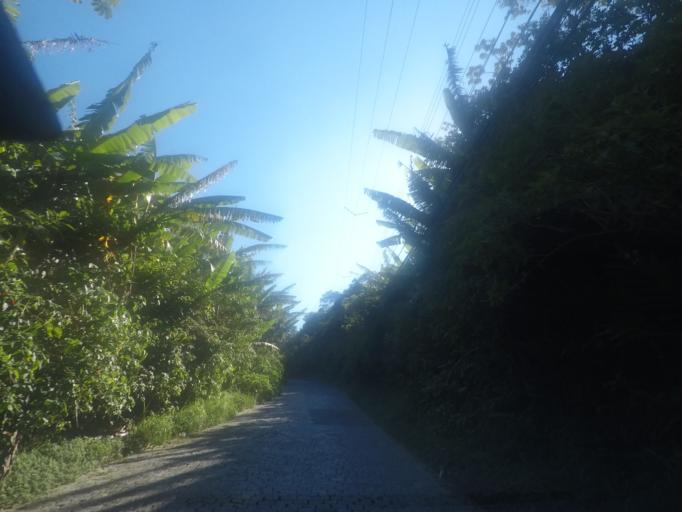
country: BR
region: Rio de Janeiro
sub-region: Petropolis
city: Petropolis
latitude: -22.5387
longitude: -43.2005
